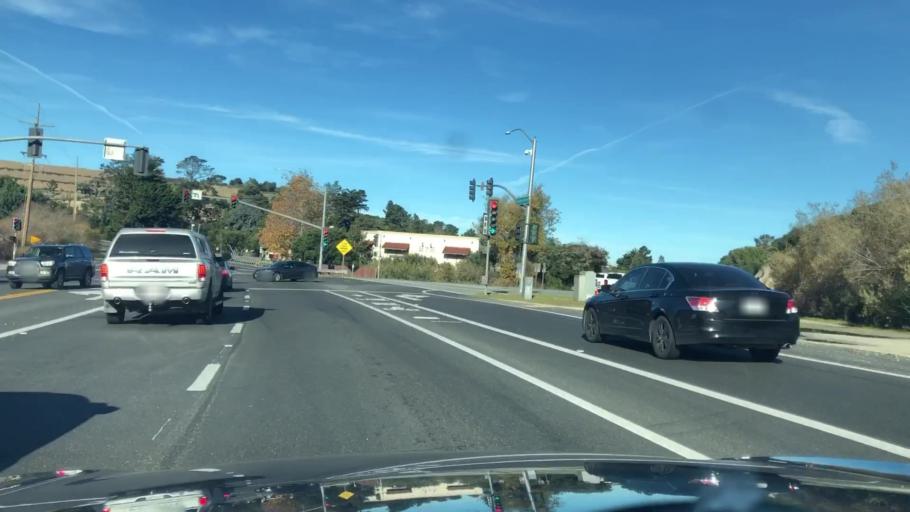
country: US
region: California
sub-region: Monterey County
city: Del Rey Oaks
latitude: 36.5806
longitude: -121.8274
